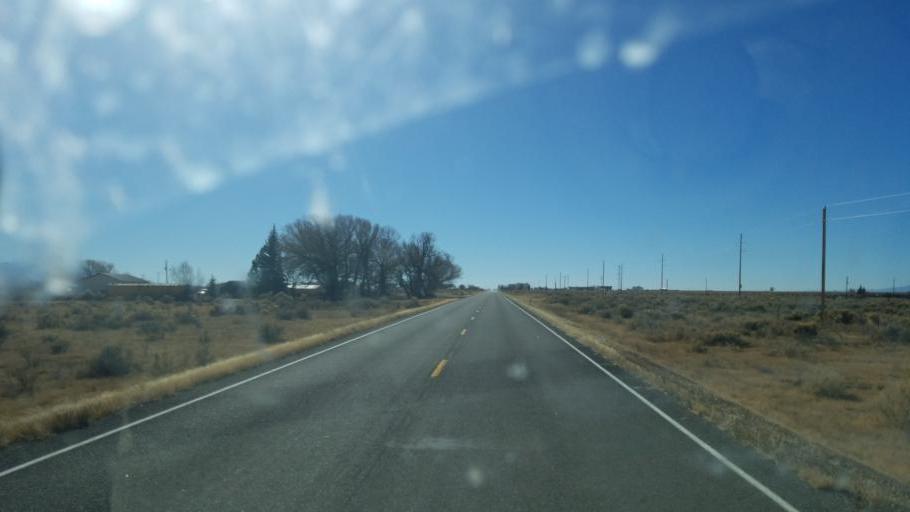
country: US
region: Colorado
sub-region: Saguache County
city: Saguache
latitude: 38.0156
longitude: -105.9104
